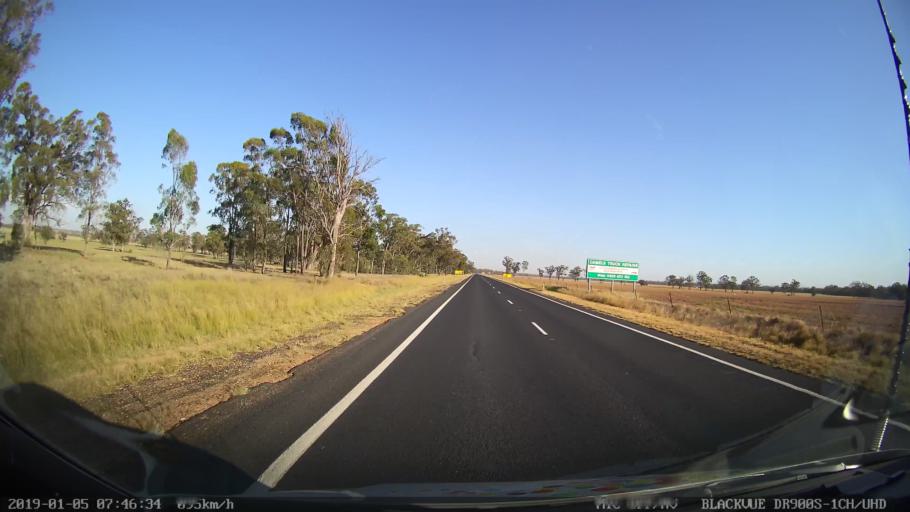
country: AU
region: New South Wales
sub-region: Gilgandra
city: Gilgandra
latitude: -31.8427
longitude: 148.6428
